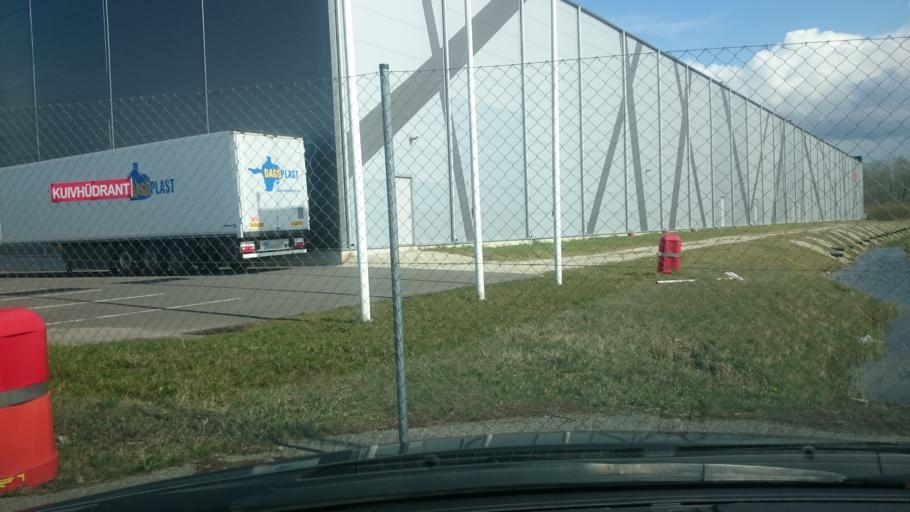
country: EE
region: Harju
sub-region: Rae vald
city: Jueri
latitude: 59.3625
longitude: 24.8694
